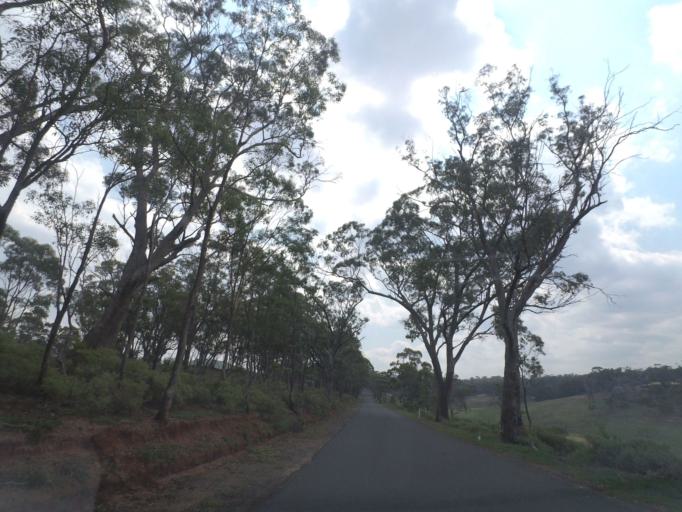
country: AU
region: Victoria
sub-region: Moorabool
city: Bacchus Marsh
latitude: -37.6137
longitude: 144.4389
